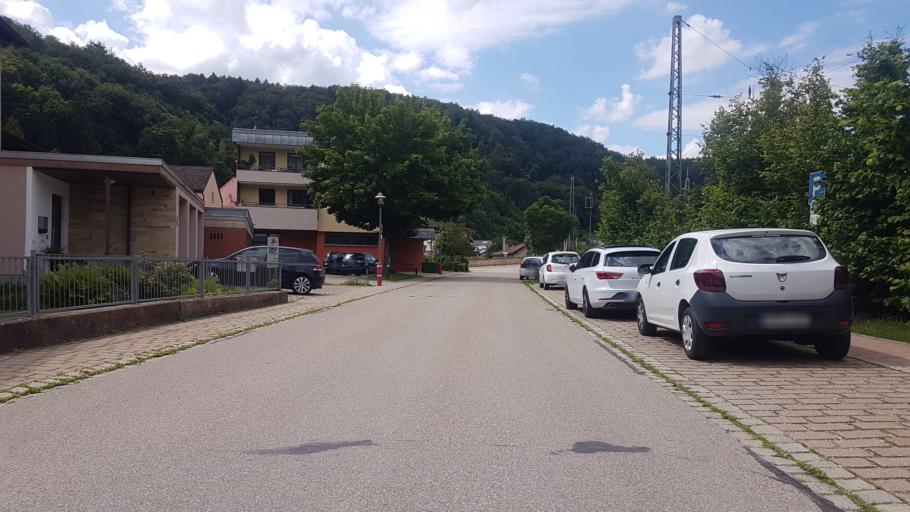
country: DE
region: Bavaria
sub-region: Regierungsbezirk Mittelfranken
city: Solnhofen
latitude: 48.8929
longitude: 10.9920
